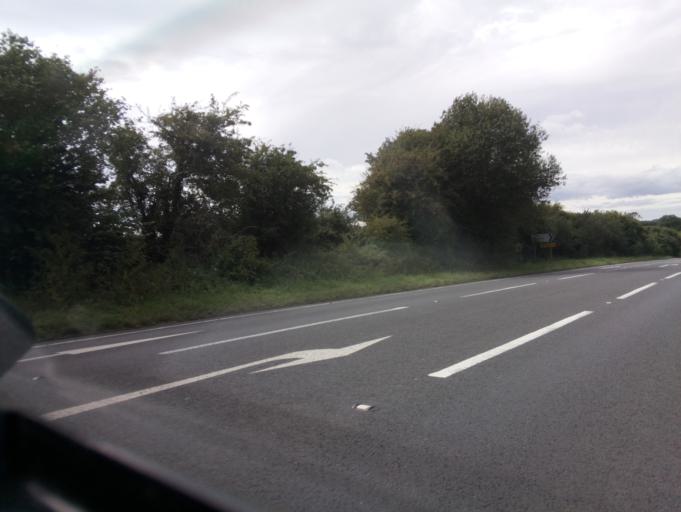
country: GB
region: England
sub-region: Somerset
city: Yeovil
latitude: 50.8859
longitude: -2.6083
